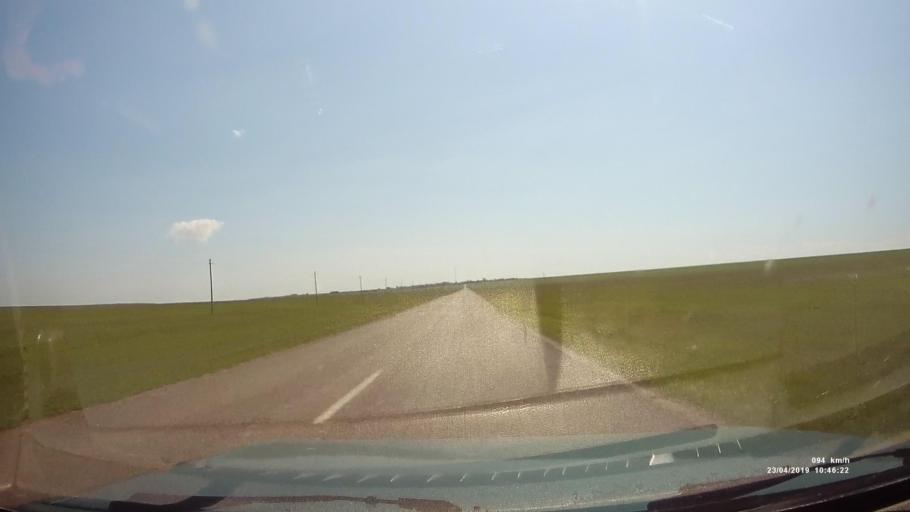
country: RU
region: Kalmykiya
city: Yashalta
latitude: 46.4436
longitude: 42.6900
